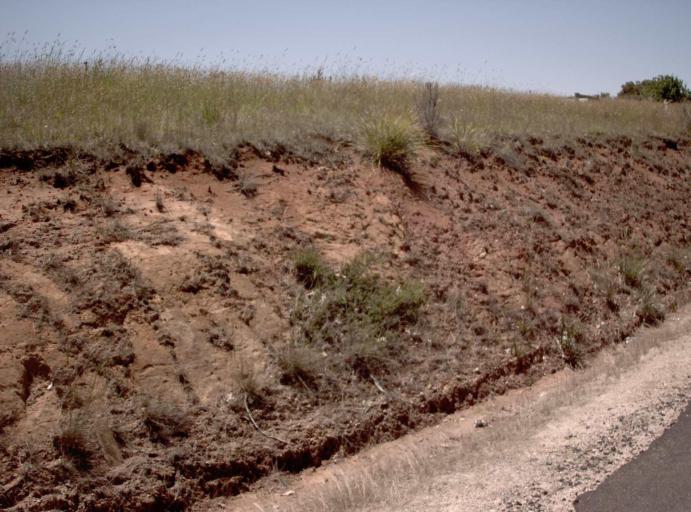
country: AU
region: Victoria
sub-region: East Gippsland
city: Lakes Entrance
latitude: -37.7526
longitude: 148.2864
